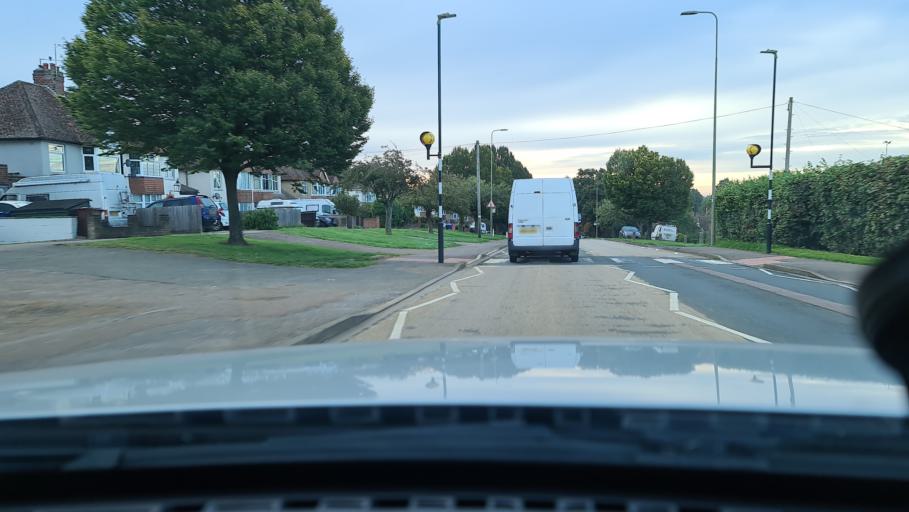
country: GB
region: England
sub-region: Oxfordshire
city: Banbury
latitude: 52.0680
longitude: -1.3594
